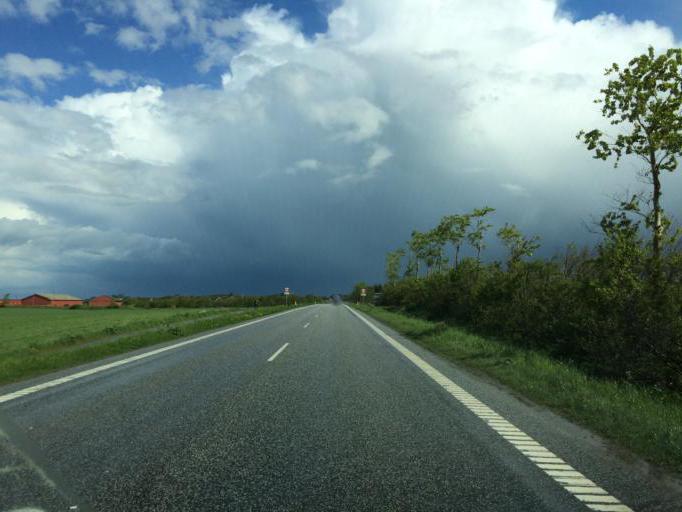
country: DK
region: Central Jutland
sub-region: Holstebro Kommune
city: Vinderup
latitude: 56.4920
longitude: 8.7876
